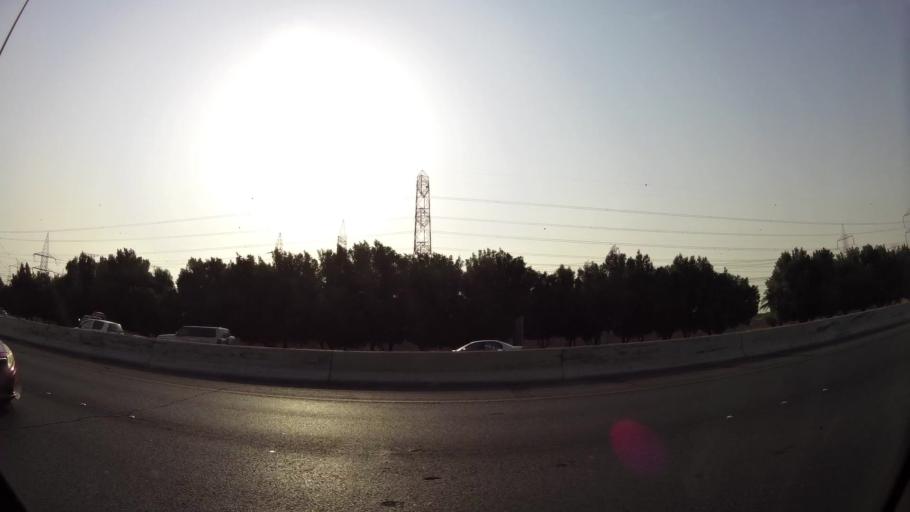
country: KW
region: Mubarak al Kabir
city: Sabah as Salim
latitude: 29.2437
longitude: 48.0489
